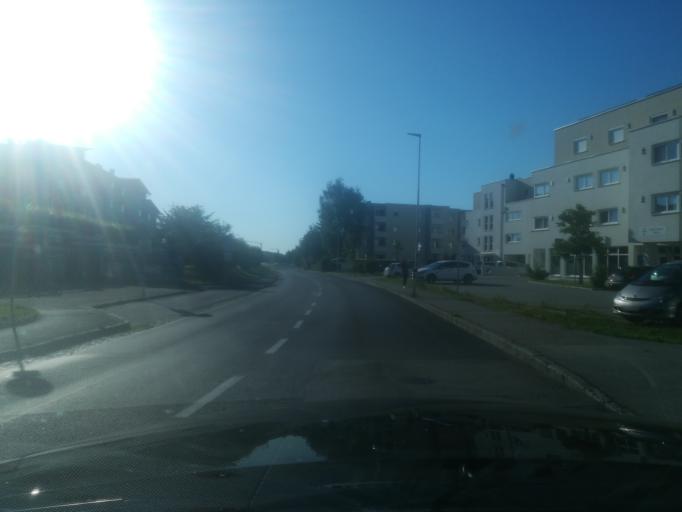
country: AT
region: Upper Austria
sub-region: Politischer Bezirk Urfahr-Umgebung
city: Gallneukirchen
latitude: 48.3482
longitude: 14.4225
